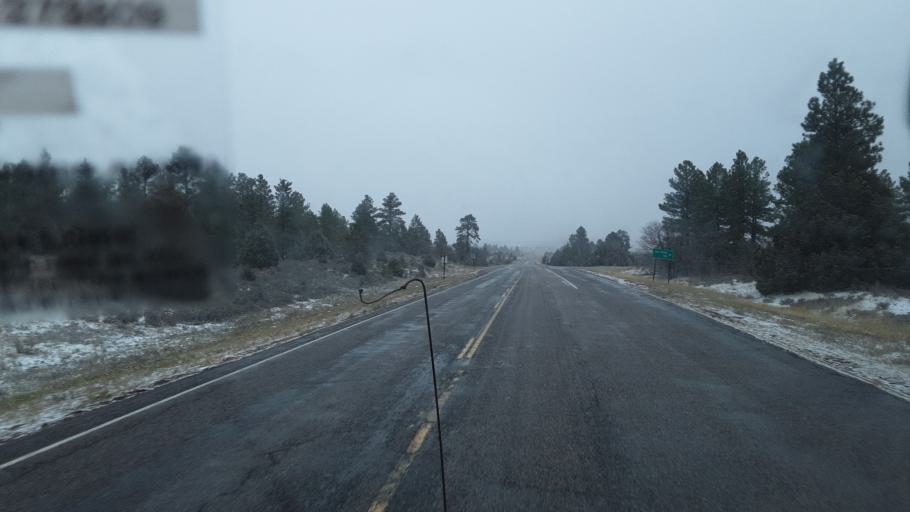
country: US
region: New Mexico
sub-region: Rio Arriba County
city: Tierra Amarilla
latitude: 36.6868
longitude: -106.5580
